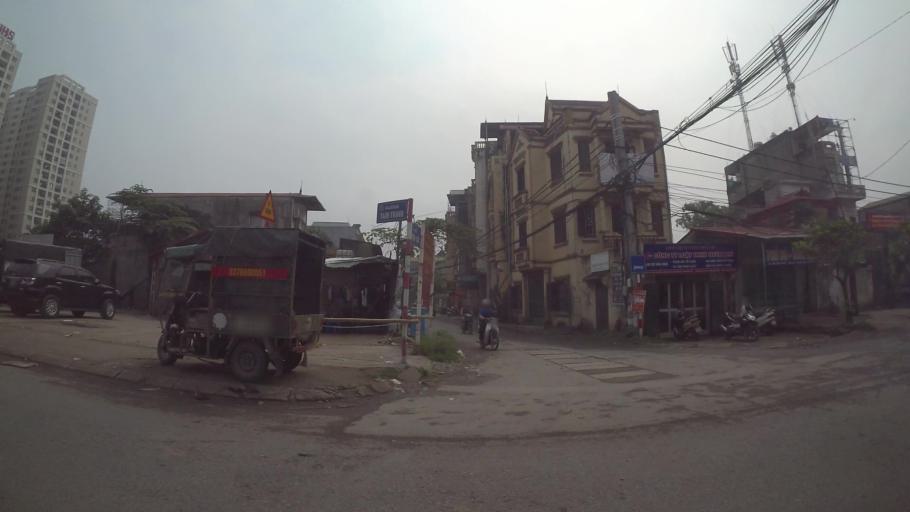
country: VN
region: Ha Noi
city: Van Dien
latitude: 20.9659
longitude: 105.8683
